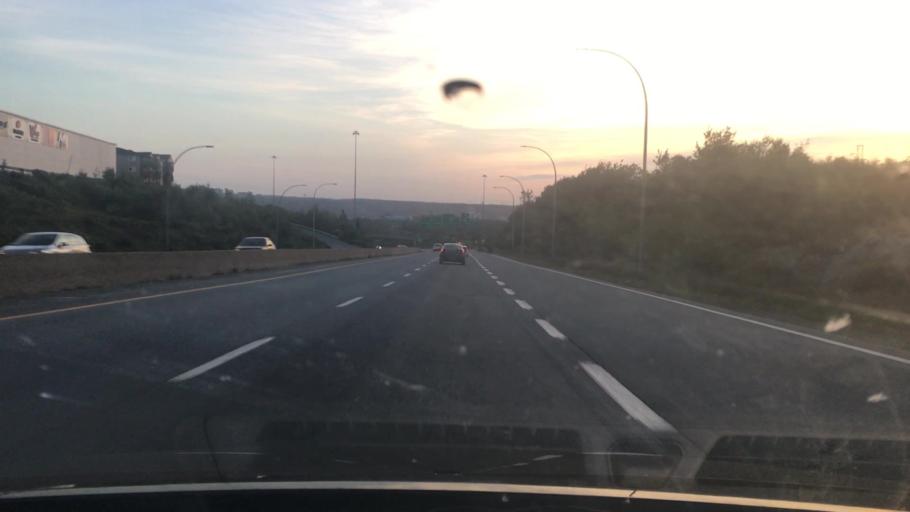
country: CA
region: Nova Scotia
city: Dartmouth
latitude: 44.6905
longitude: -63.5890
